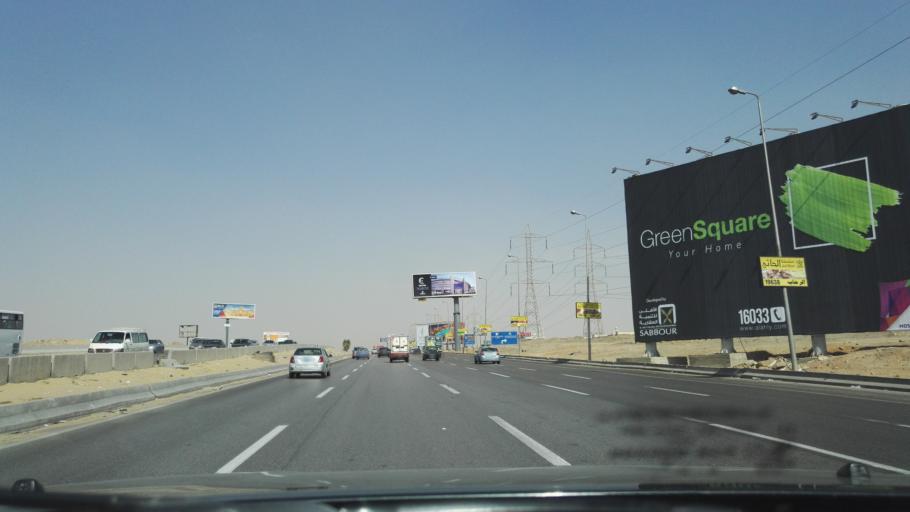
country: EG
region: Muhafazat al Qalyubiyah
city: Al Khankah
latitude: 30.0803
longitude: 31.4442
